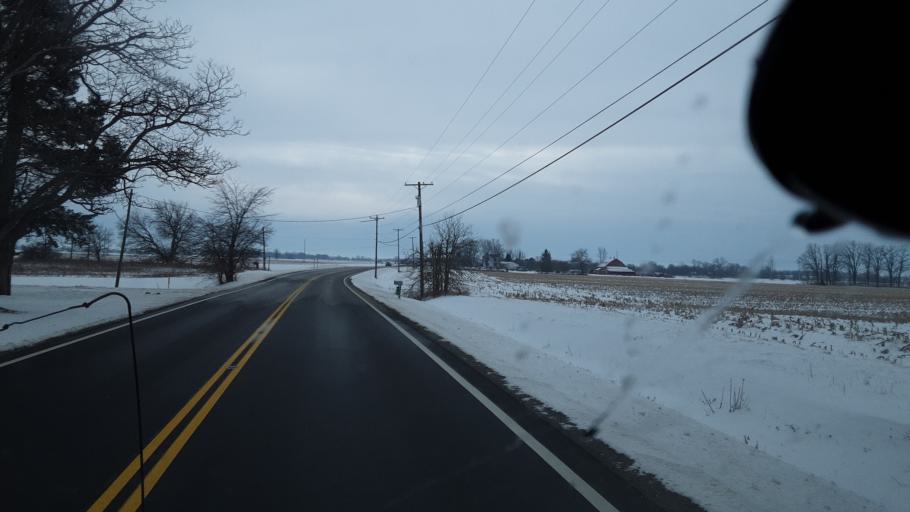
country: US
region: Ohio
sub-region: Madison County
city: London
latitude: 39.8748
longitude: -83.4559
